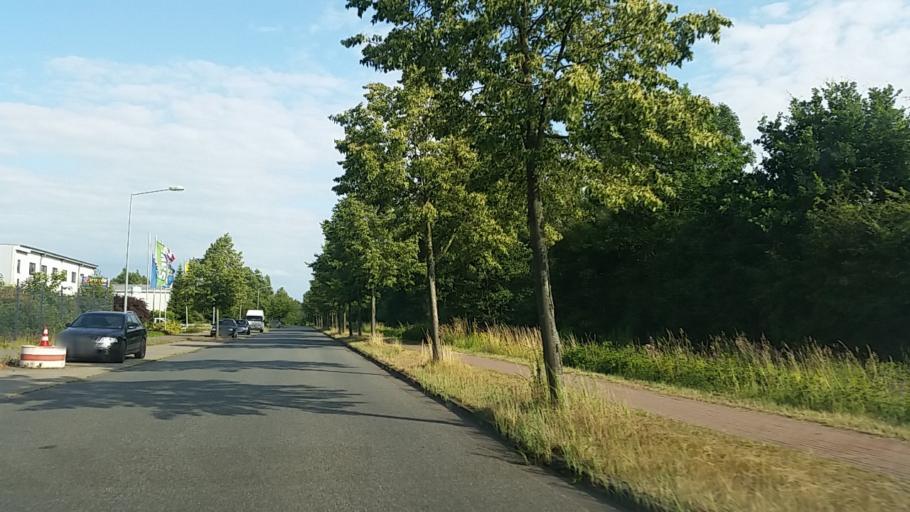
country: DE
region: Lower Saxony
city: Winsen
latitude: 53.3388
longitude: 10.2317
